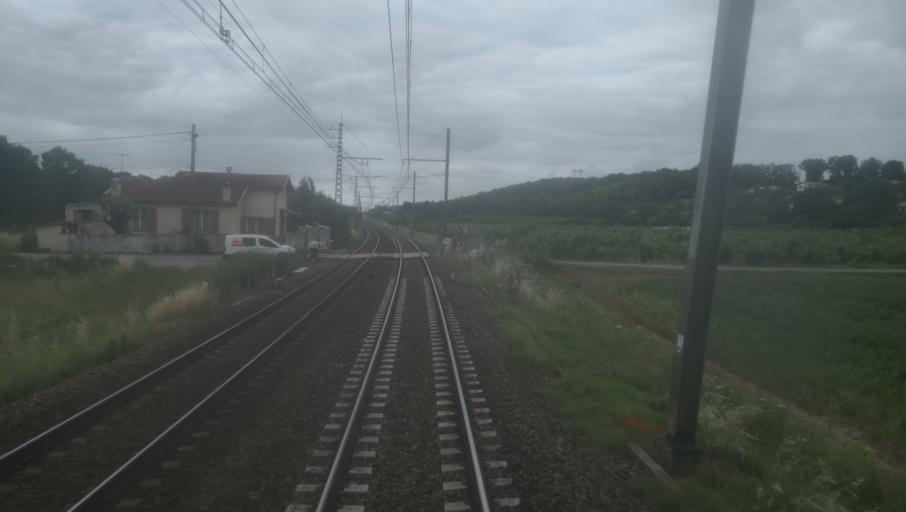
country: FR
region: Midi-Pyrenees
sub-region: Departement du Tarn-et-Garonne
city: Grisolles
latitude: 43.8504
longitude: 1.2873
